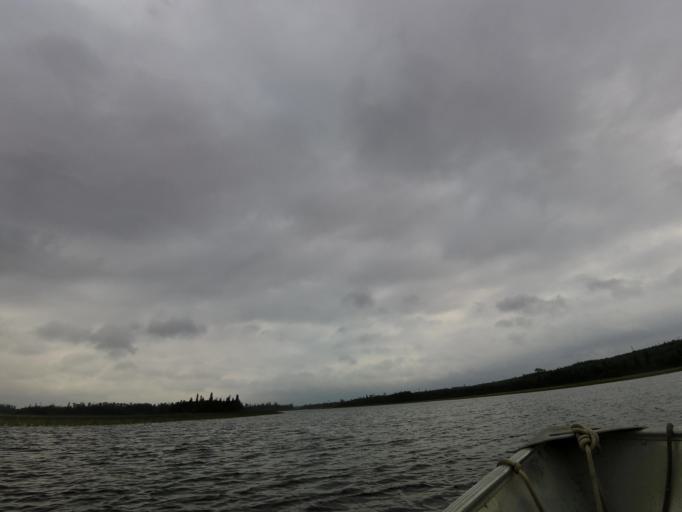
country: CA
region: Ontario
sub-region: Rainy River District
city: Atikokan
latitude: 49.5864
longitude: -91.3726
